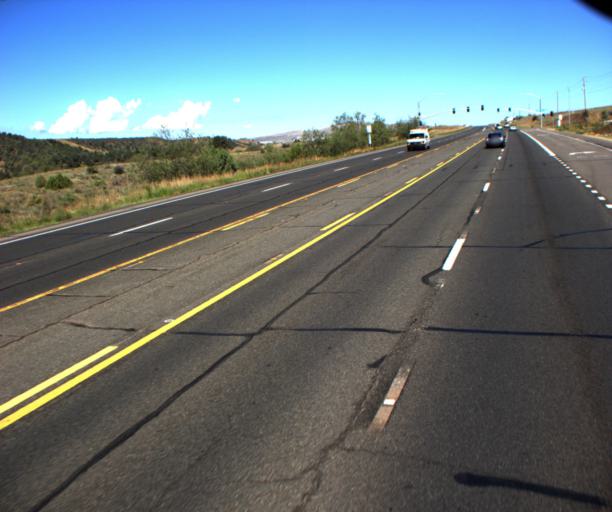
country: US
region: Arizona
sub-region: Yavapai County
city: Prescott Valley
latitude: 34.5736
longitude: -112.2801
